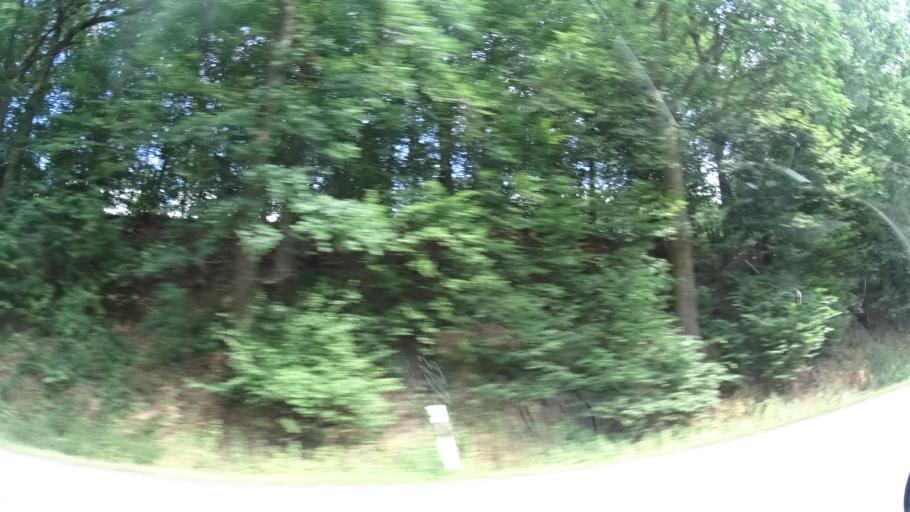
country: DE
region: Hesse
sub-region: Regierungsbezirk Kassel
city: Eiterfeld
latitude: 50.8016
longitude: 9.7353
